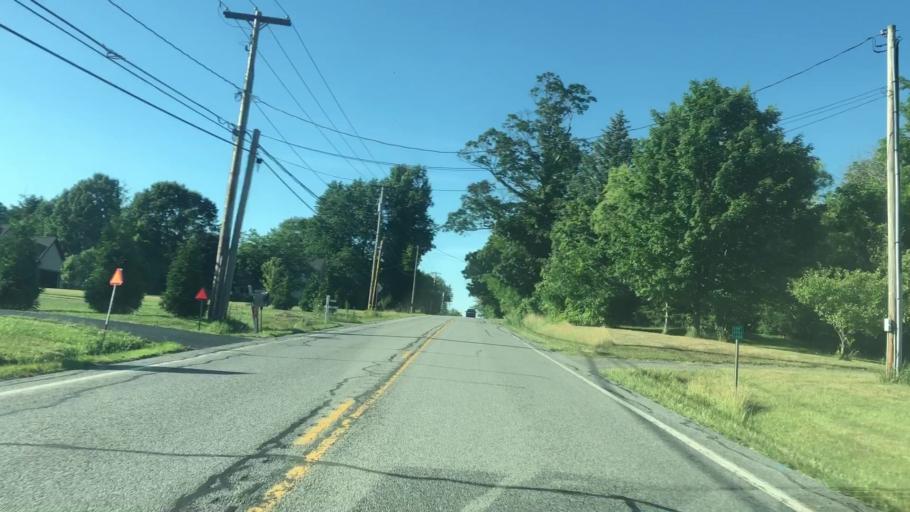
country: US
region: New York
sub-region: Wayne County
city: Ontario
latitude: 43.1490
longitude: -77.2927
